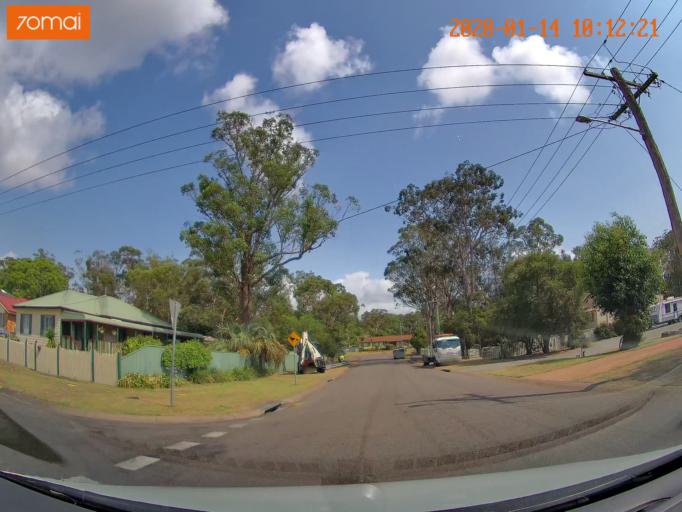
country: AU
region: New South Wales
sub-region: Lake Macquarie Shire
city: Dora Creek
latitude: -33.1165
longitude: 151.5295
